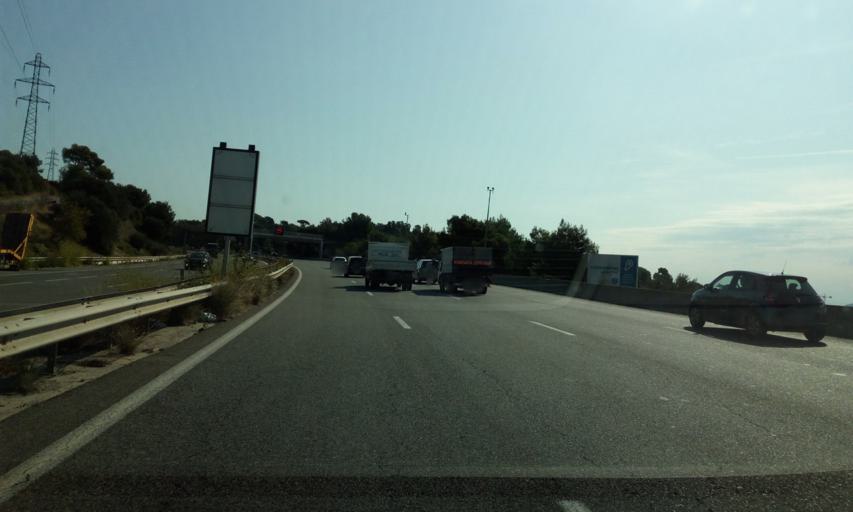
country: FR
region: Provence-Alpes-Cote d'Azur
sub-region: Departement du Var
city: Ollioules
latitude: 43.1194
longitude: 5.8619
